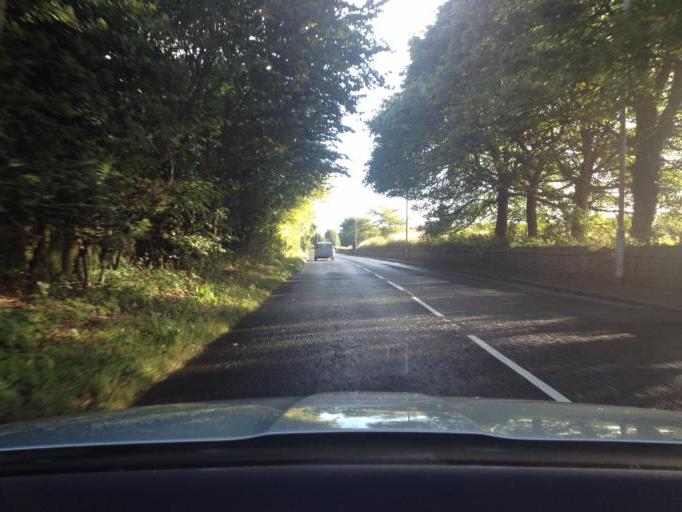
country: GB
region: Scotland
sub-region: West Lothian
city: Mid Calder
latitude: 55.8927
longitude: -3.4752
